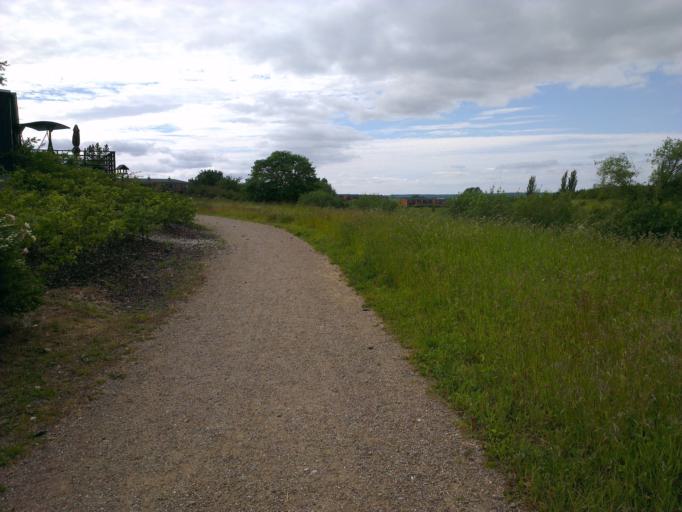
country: DK
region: Capital Region
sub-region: Frederikssund Kommune
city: Frederikssund
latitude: 55.8655
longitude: 12.0759
